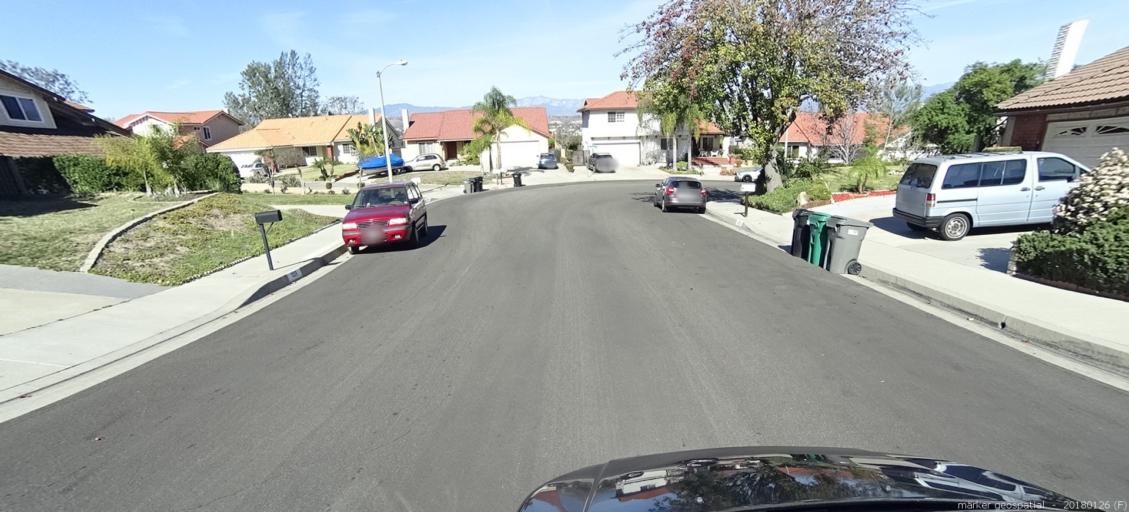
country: US
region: California
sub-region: Los Angeles County
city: Walnut
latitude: 33.9971
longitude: -117.8451
